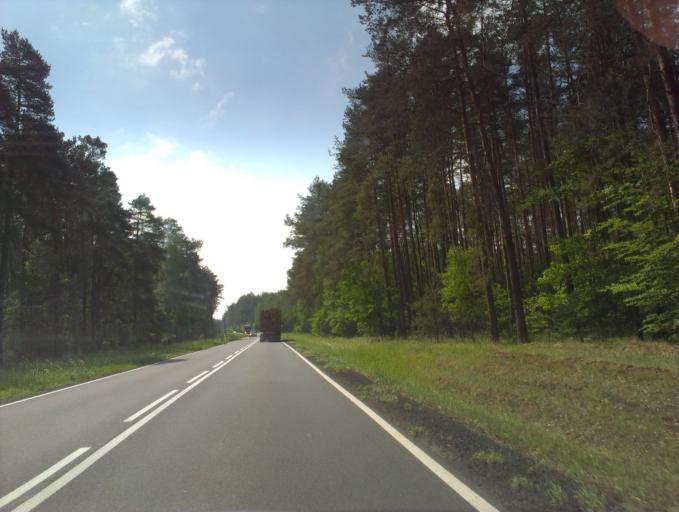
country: PL
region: Greater Poland Voivodeship
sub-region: Powiat zlotowski
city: Tarnowka
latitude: 53.3474
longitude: 16.7894
